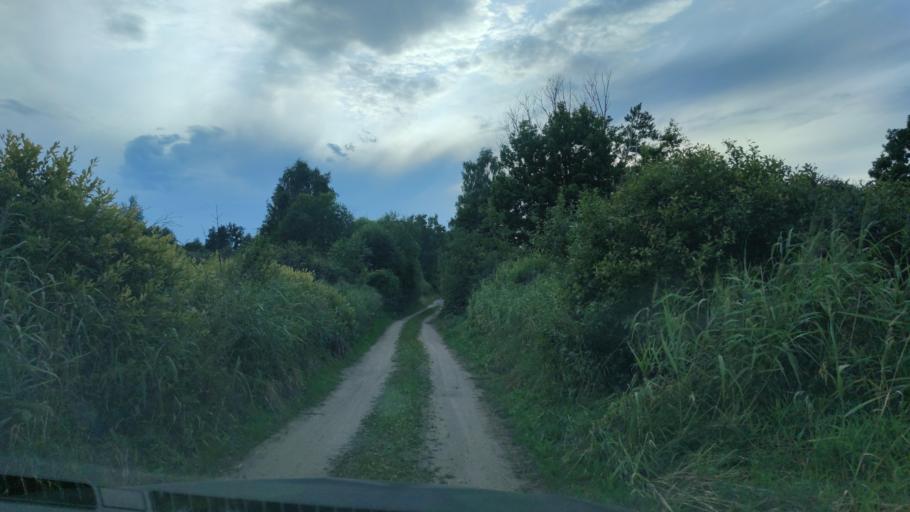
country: BY
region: Vitebsk
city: Mosar
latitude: 55.1228
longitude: 27.1811
